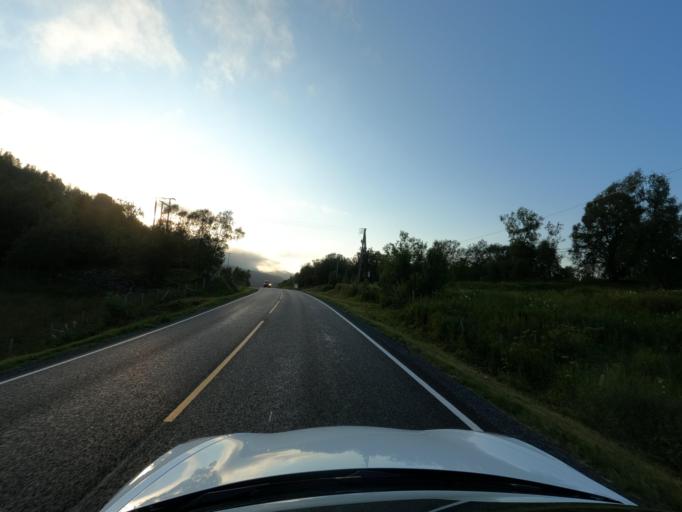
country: NO
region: Troms
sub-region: Skanland
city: Evenskjer
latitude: 68.6746
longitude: 16.5668
